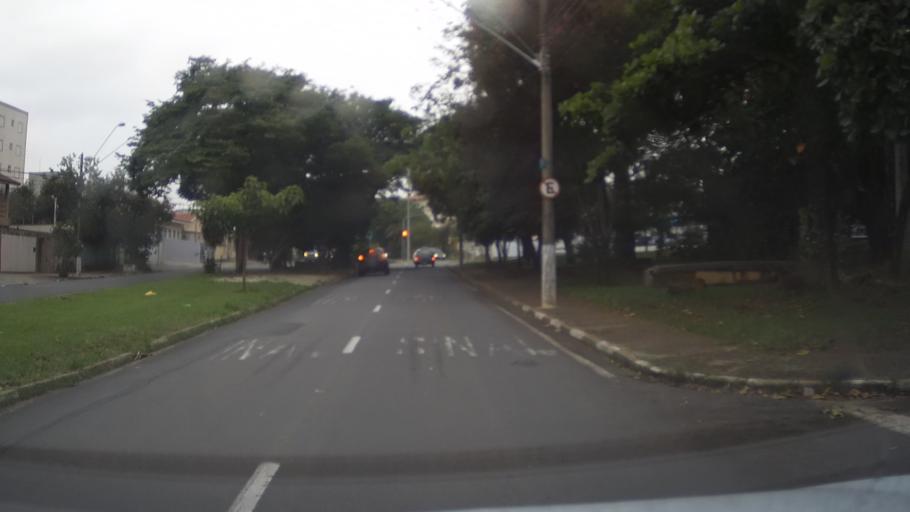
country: BR
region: Sao Paulo
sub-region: Campinas
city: Campinas
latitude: -22.9312
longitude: -47.0408
